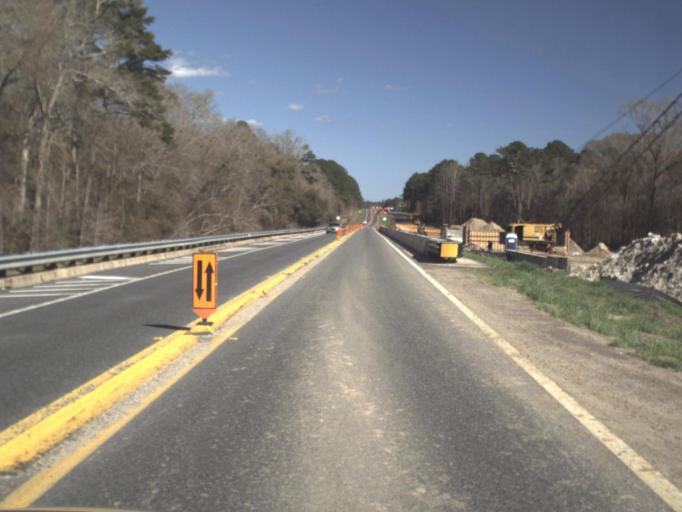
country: US
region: Florida
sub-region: Gadsden County
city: Quincy
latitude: 30.5536
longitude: -84.5120
